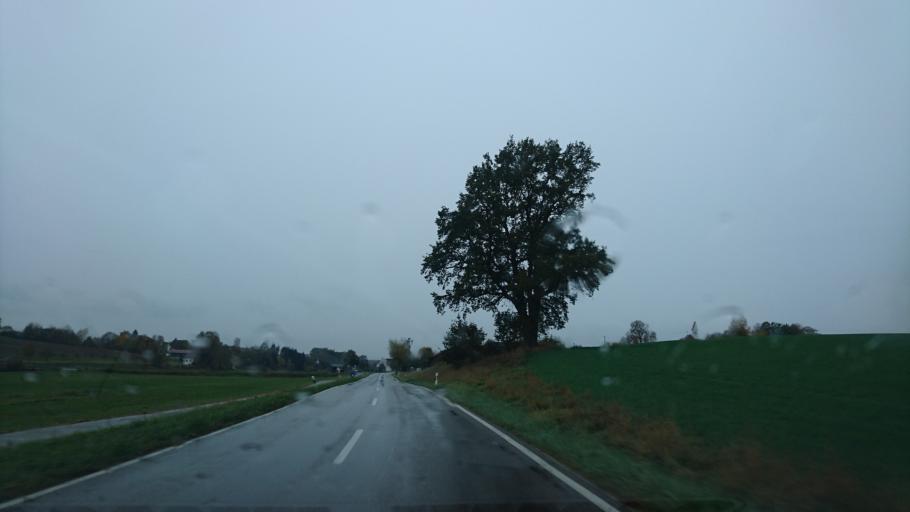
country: DE
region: Bavaria
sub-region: Upper Bavaria
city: Hilgertshausen-Tandern
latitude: 48.4292
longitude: 11.3692
